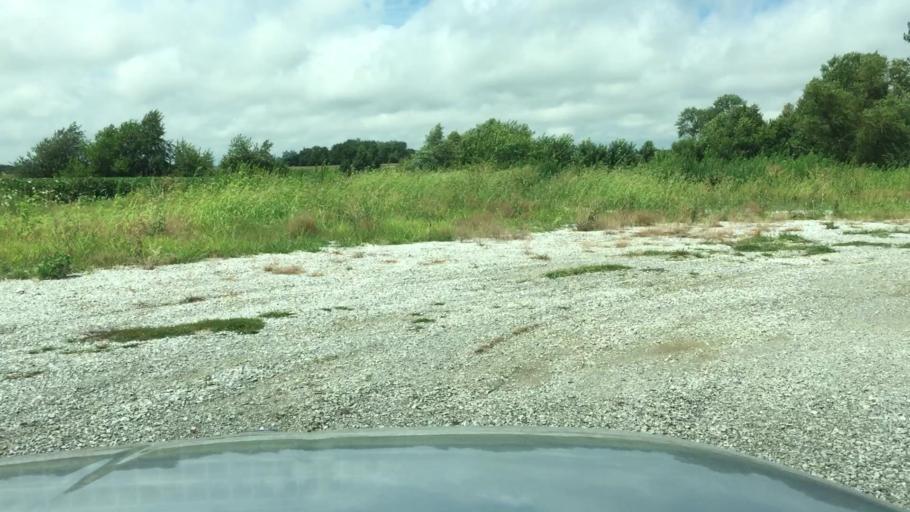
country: US
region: Illinois
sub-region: Hancock County
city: Nauvoo
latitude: 40.5507
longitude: -91.3302
